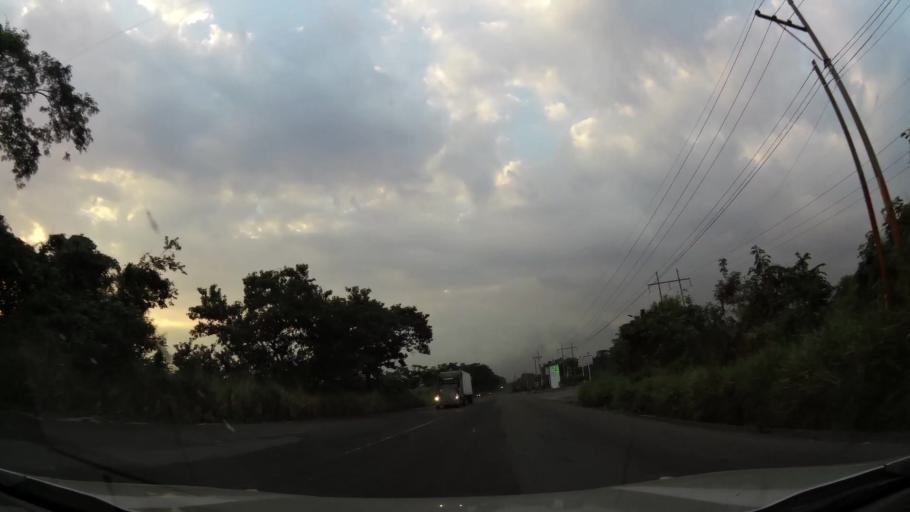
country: GT
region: Escuintla
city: Siquinala
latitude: 14.2772
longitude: -90.9197
